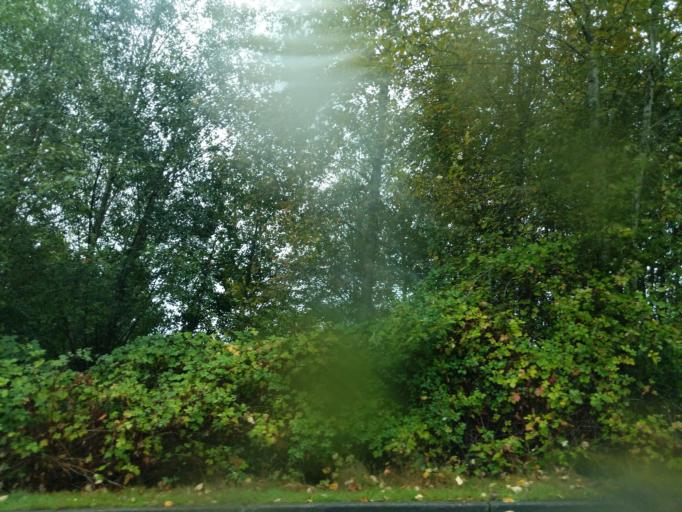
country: US
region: Washington
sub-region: Snohomish County
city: North Creek
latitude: 47.7973
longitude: -122.1960
